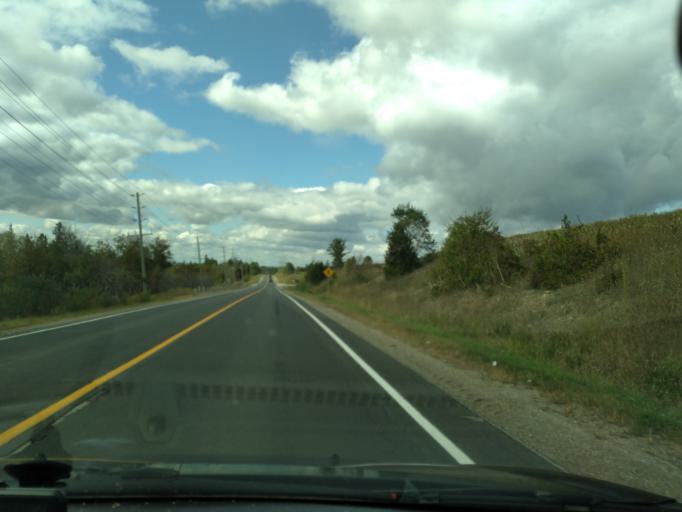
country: CA
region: Ontario
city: Innisfil
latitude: 44.2614
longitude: -79.7652
